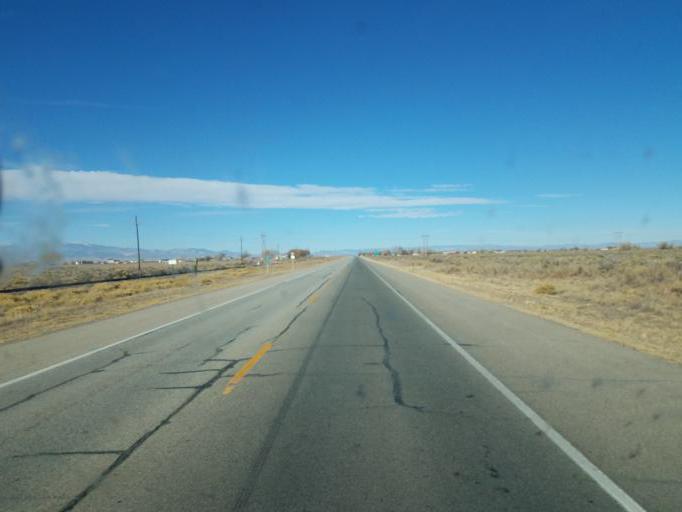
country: US
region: Colorado
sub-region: Alamosa County
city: Alamosa
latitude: 37.4988
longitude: -105.9502
